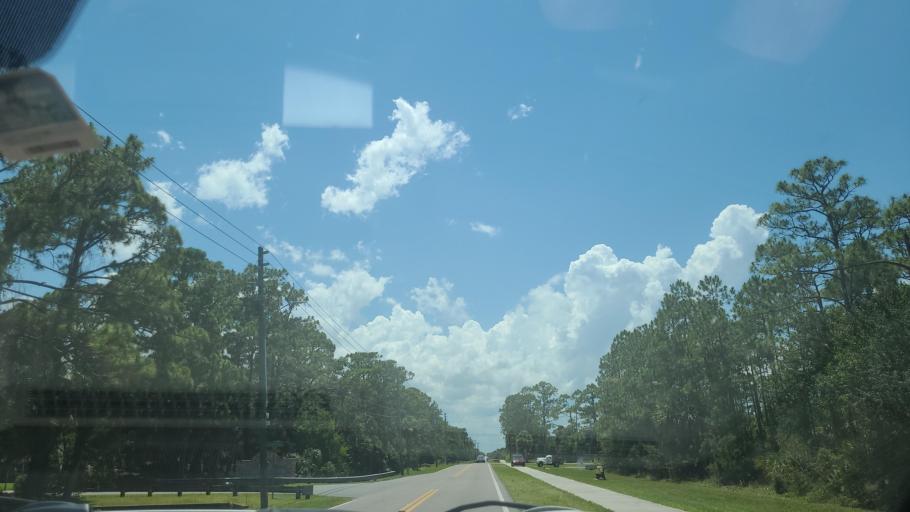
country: US
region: Florida
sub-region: Brevard County
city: Grant-Valkaria
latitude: 27.9537
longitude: -80.5842
